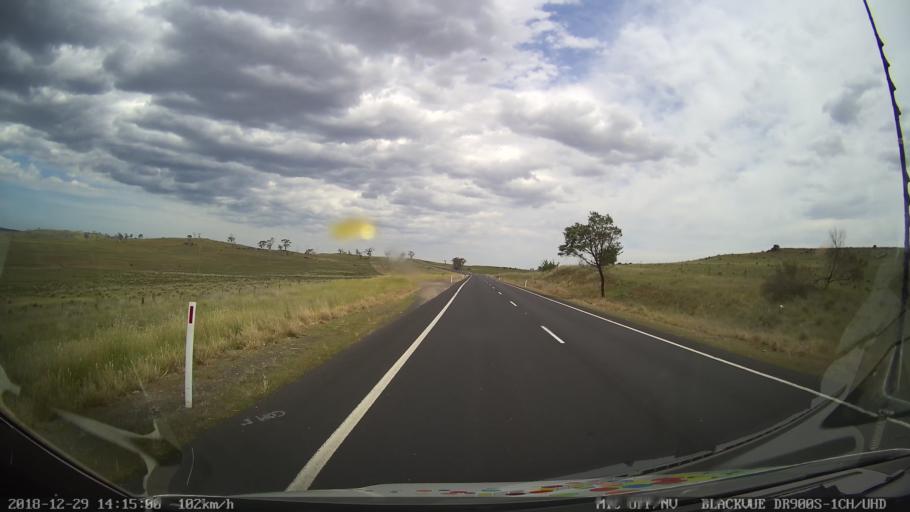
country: AU
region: New South Wales
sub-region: Cooma-Monaro
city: Cooma
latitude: -36.4500
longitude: 149.2374
